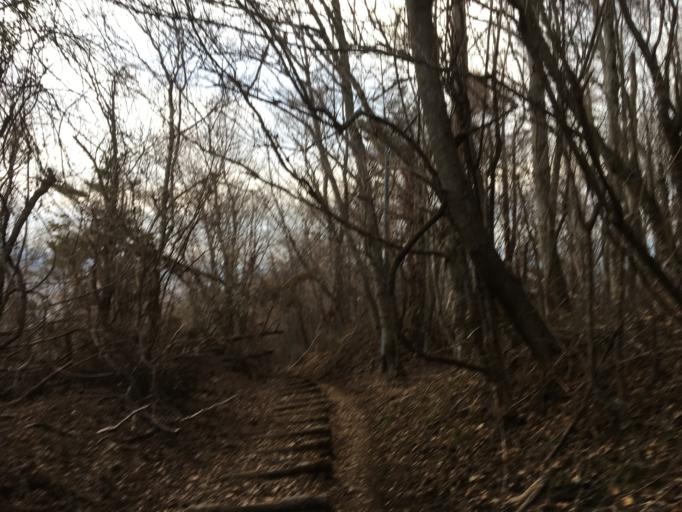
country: JP
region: Shizuoka
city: Gotemba
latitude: 35.4371
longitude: 138.8664
